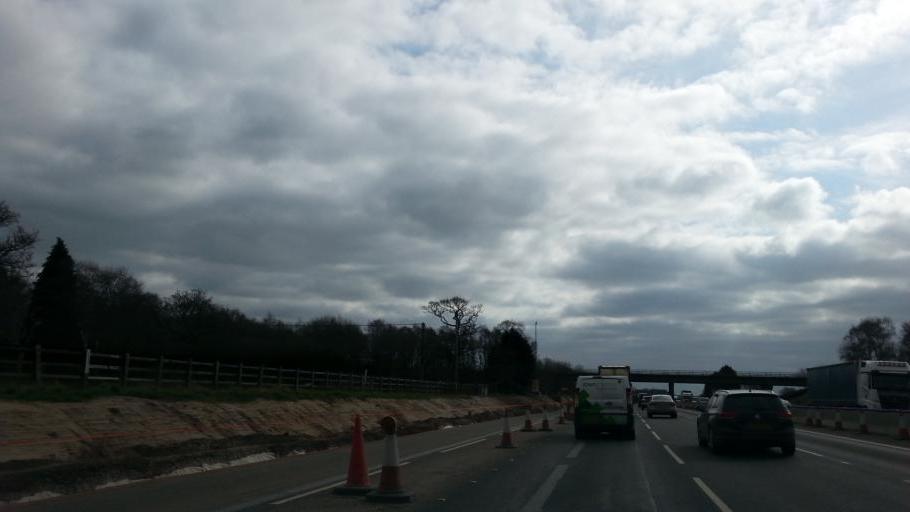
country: GB
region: England
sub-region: Cheshire East
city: Holmes Chapel
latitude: 53.2188
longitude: -2.3900
